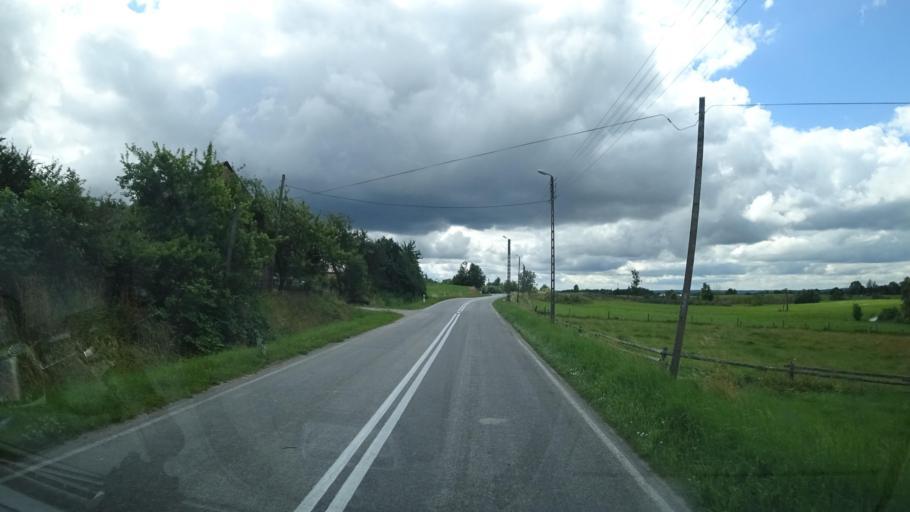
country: PL
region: Warmian-Masurian Voivodeship
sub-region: Powiat goldapski
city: Goldap
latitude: 54.2233
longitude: 22.2338
